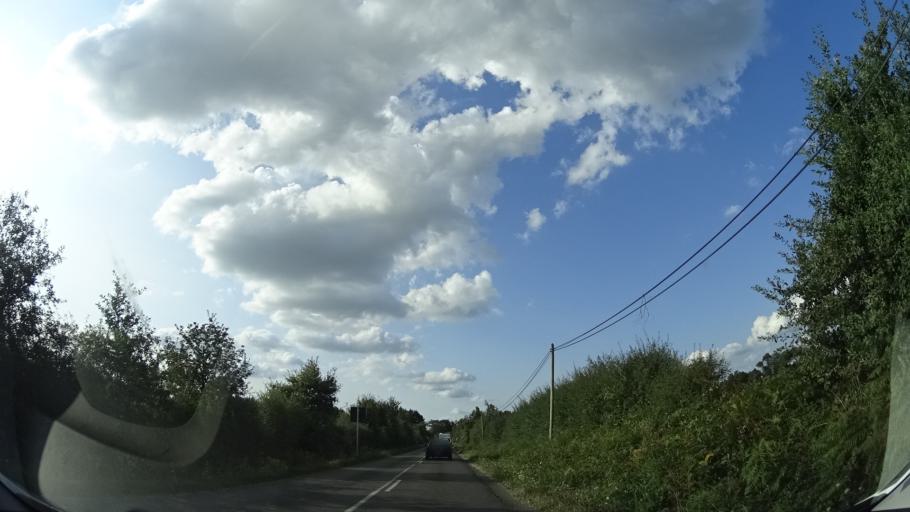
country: FR
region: Pays de la Loire
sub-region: Departement de la Loire-Atlantique
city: Casson
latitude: 47.3970
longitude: -1.5270
